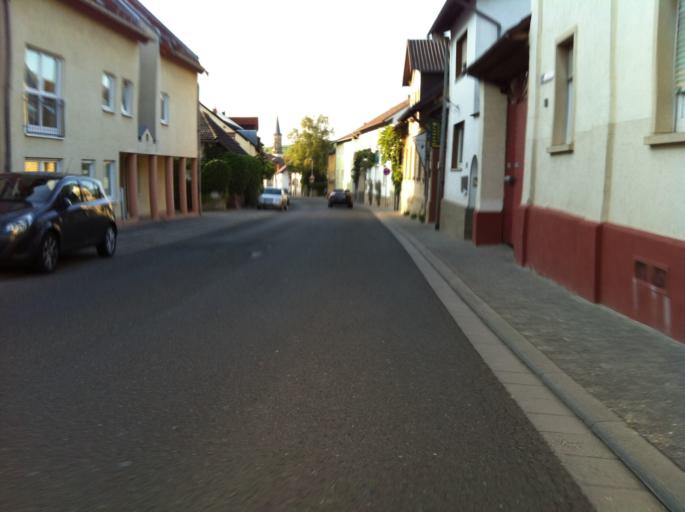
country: DE
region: Rheinland-Pfalz
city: Schwabenheim
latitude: 49.9289
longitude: 8.0987
